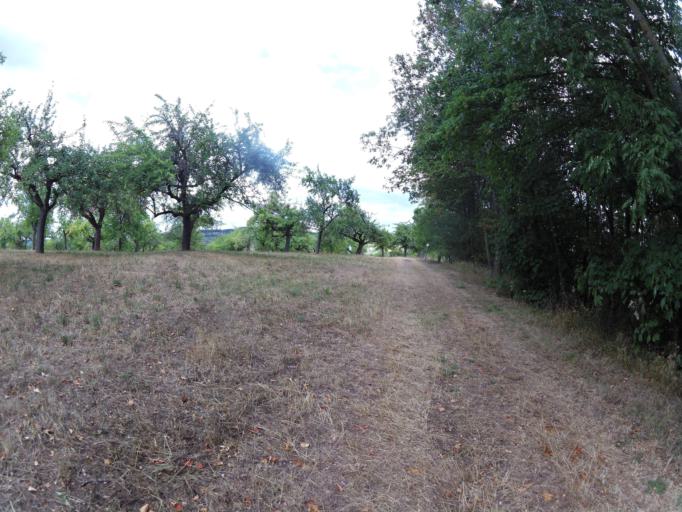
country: DE
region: Bavaria
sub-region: Regierungsbezirk Unterfranken
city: Thungersheim
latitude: 49.8796
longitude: 9.8298
